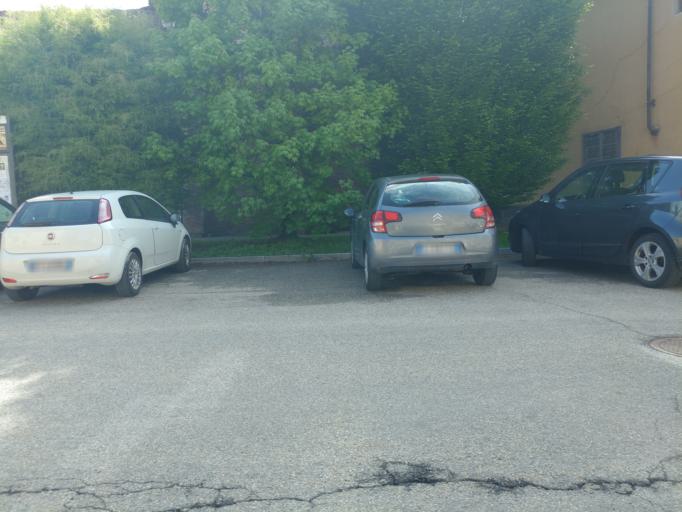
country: IT
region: Piedmont
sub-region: Provincia di Torino
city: Pancalieri
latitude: 44.8305
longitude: 7.5897
